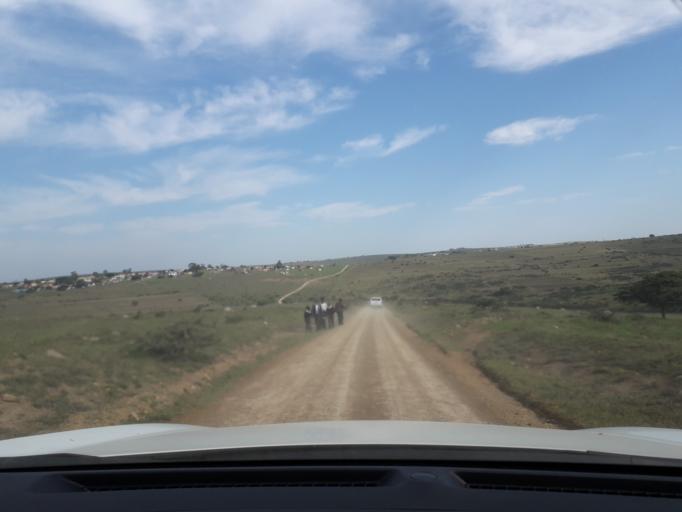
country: ZA
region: Eastern Cape
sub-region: Buffalo City Metropolitan Municipality
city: Bhisho
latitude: -32.9938
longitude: 27.3439
